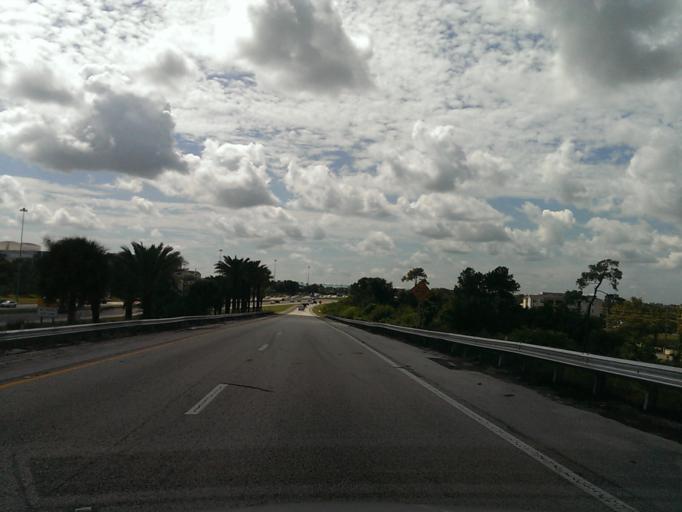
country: US
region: Florida
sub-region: Orange County
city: Williamsburg
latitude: 28.4200
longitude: -81.4753
